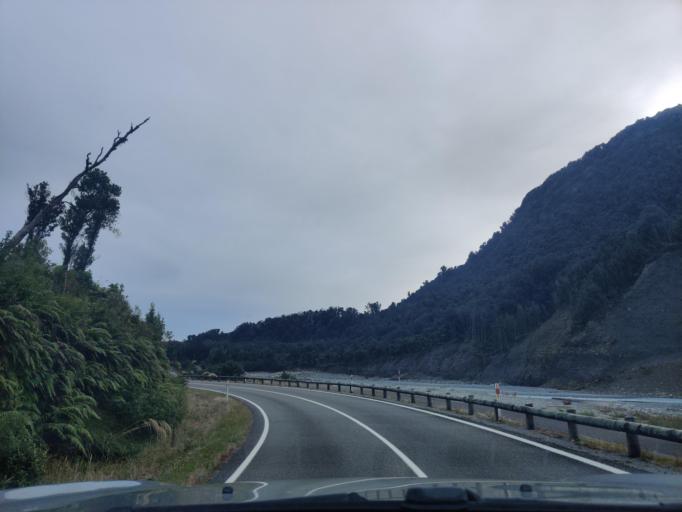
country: NZ
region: West Coast
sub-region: Westland District
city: Hokitika
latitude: -43.3981
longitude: 170.1815
